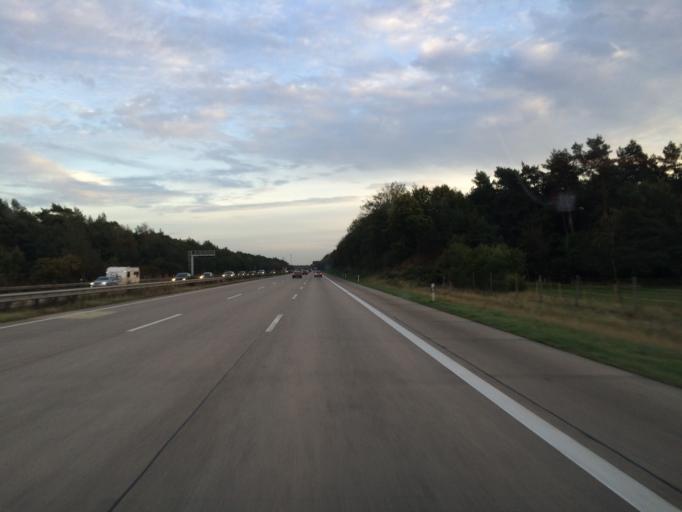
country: DE
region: Lower Saxony
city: Elze
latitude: 52.6078
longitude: 9.7399
